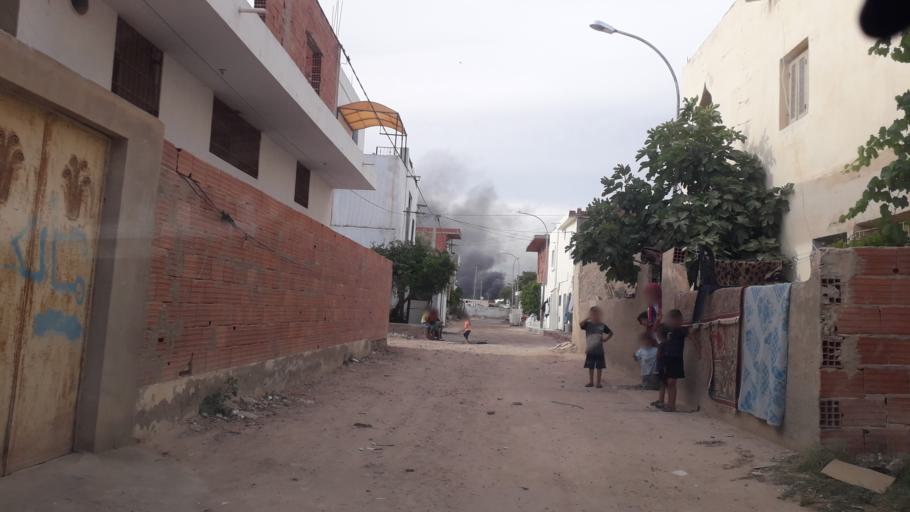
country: TN
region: Safaqis
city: Al Qarmadah
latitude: 34.8863
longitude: 10.7598
